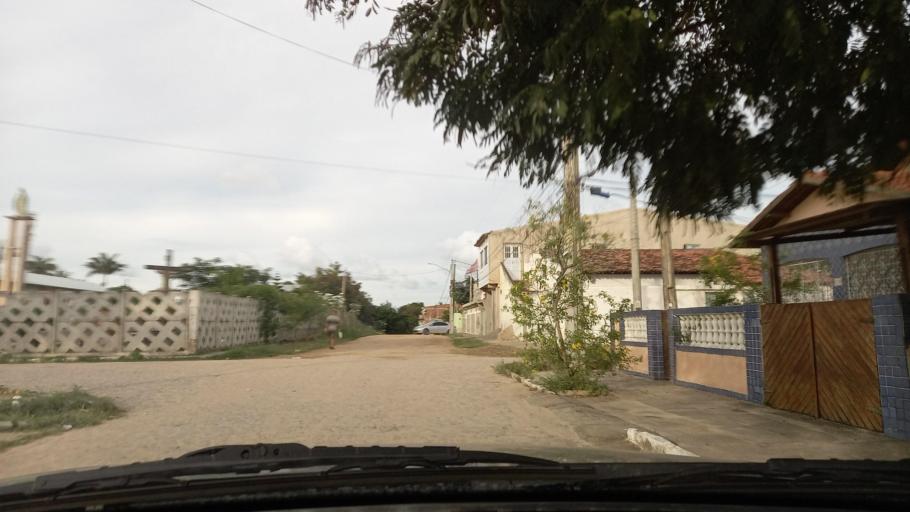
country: BR
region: Pernambuco
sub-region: Gravata
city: Gravata
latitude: -8.1977
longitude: -35.5544
